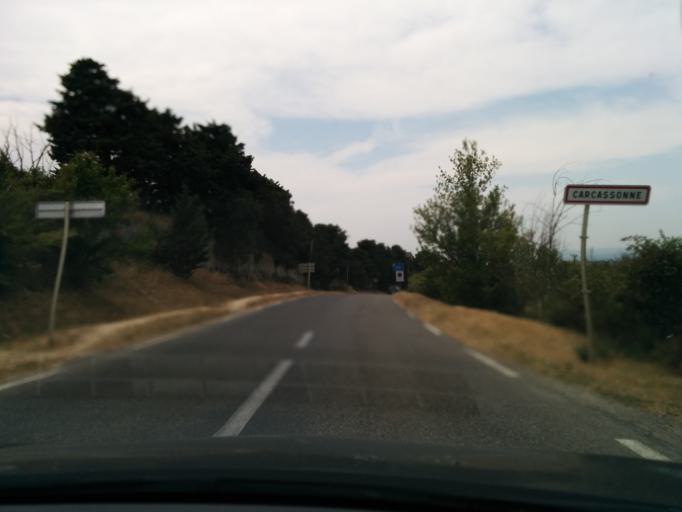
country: FR
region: Languedoc-Roussillon
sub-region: Departement de l'Aude
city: Cazilhac
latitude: 43.2040
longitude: 2.3733
